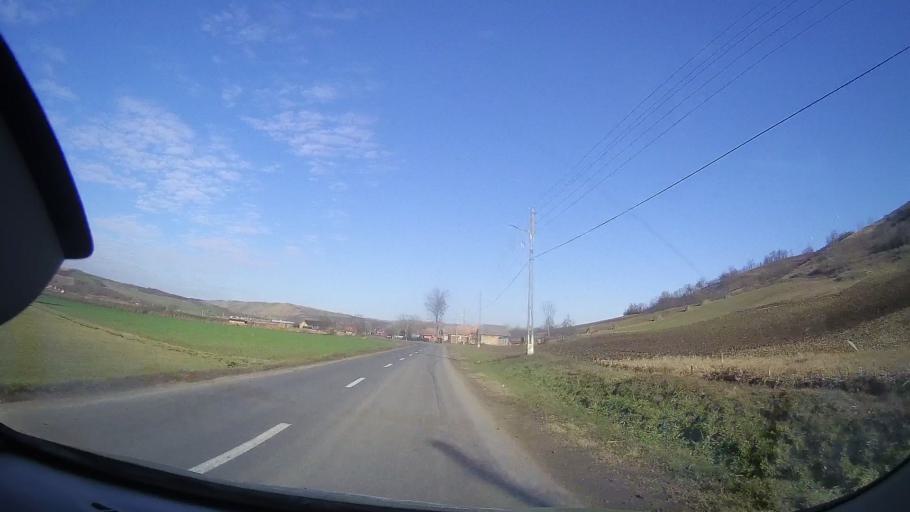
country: RO
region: Mures
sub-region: Comuna Band
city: Band
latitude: 46.5548
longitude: 24.3353
